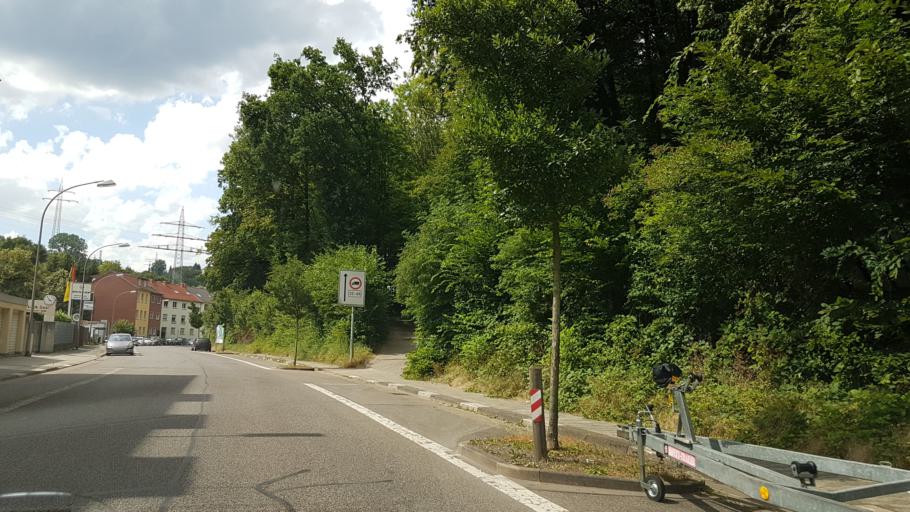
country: DE
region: Saarland
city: Saarbrucken
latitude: 49.2520
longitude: 6.9777
